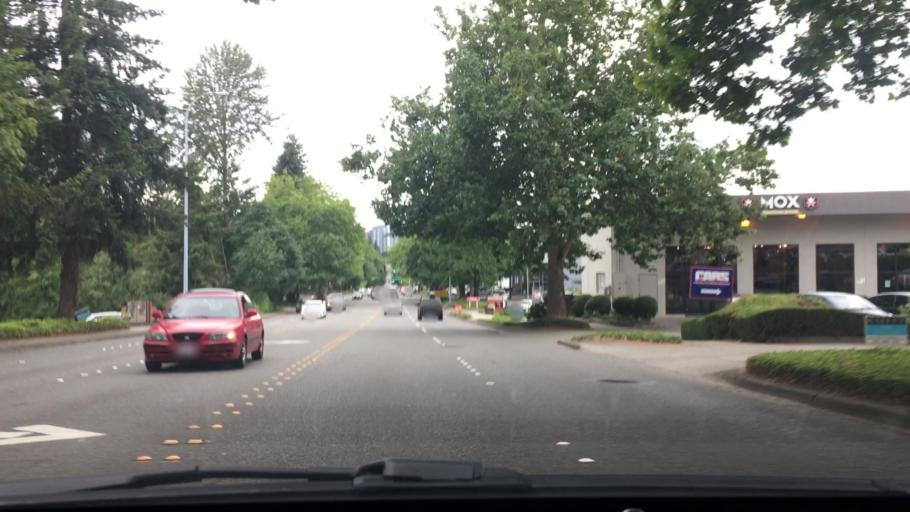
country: US
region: Washington
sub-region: King County
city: Bellevue
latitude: 47.6226
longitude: -122.1620
